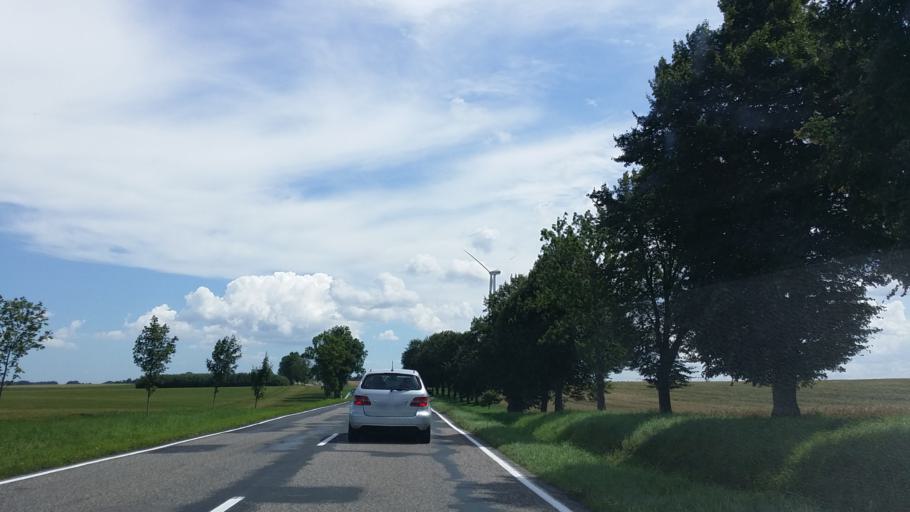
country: PL
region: West Pomeranian Voivodeship
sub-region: Powiat kolobrzeski
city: Ustronie Morskie
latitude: 54.2024
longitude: 15.8695
